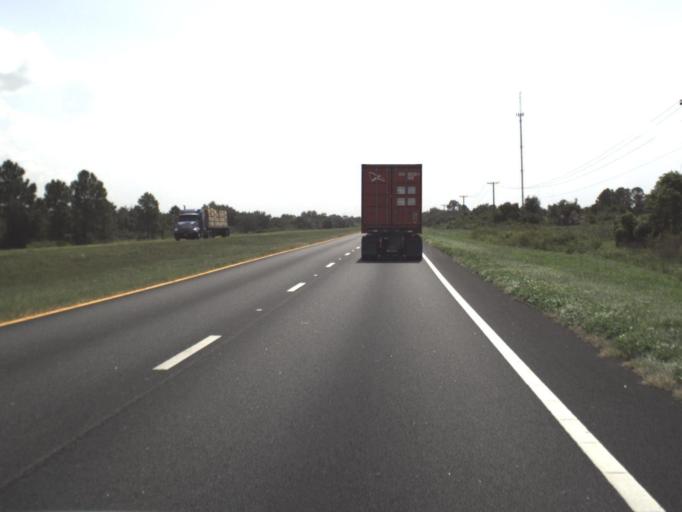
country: US
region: Florida
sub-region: Polk County
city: Frostproof
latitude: 27.6739
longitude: -81.5509
